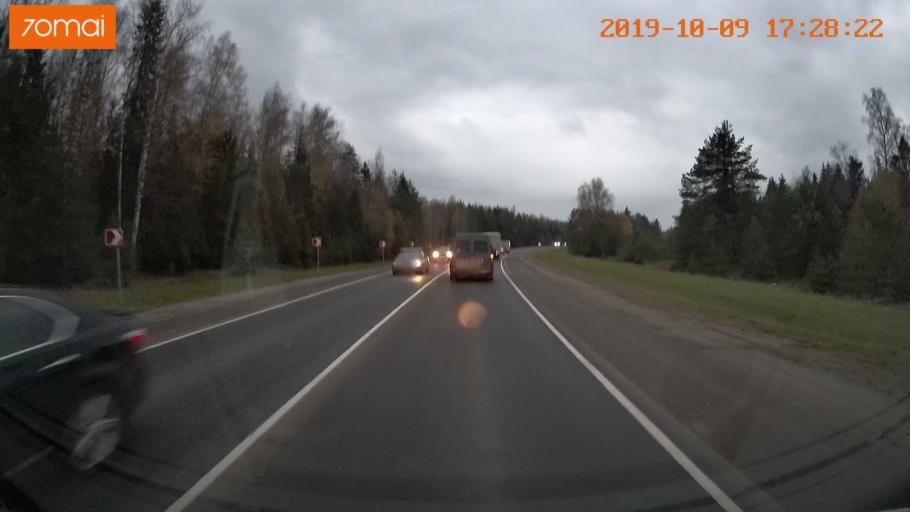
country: RU
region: Ivanovo
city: Furmanov
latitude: 57.1584
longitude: 41.0685
